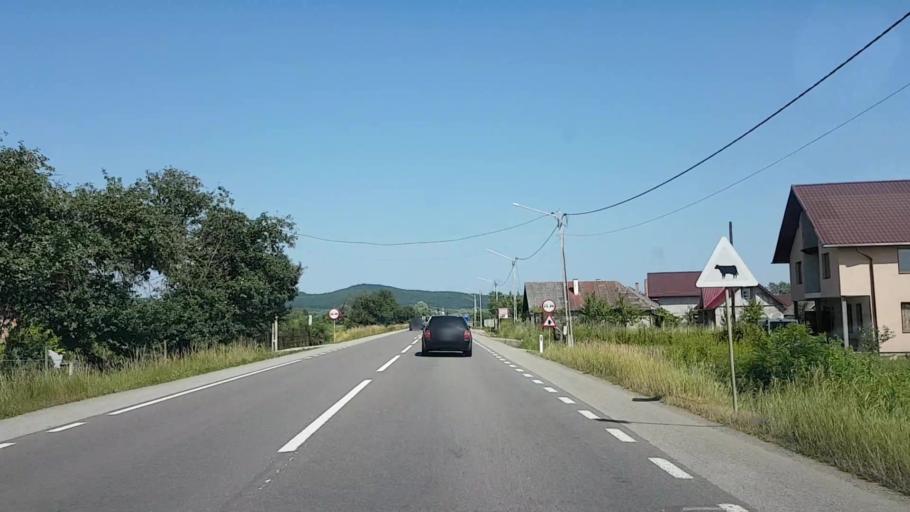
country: RO
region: Bistrita-Nasaud
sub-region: Comuna Sintereag
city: Sintereag
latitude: 47.1810
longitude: 24.2655
